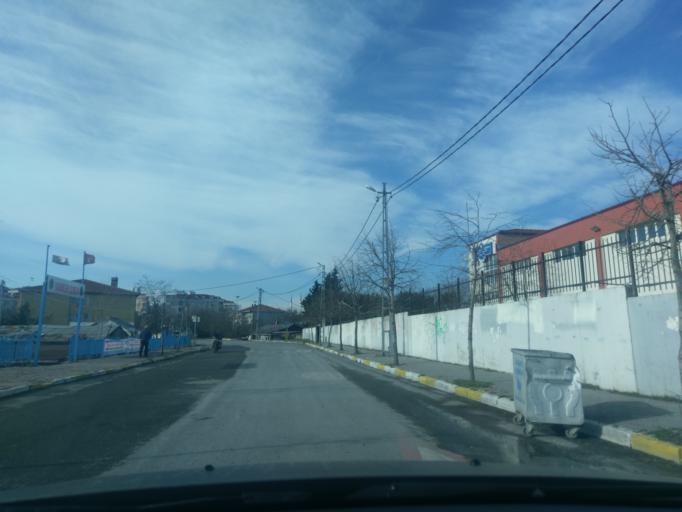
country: TR
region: Istanbul
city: Sultangazi
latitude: 41.1338
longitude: 28.8415
